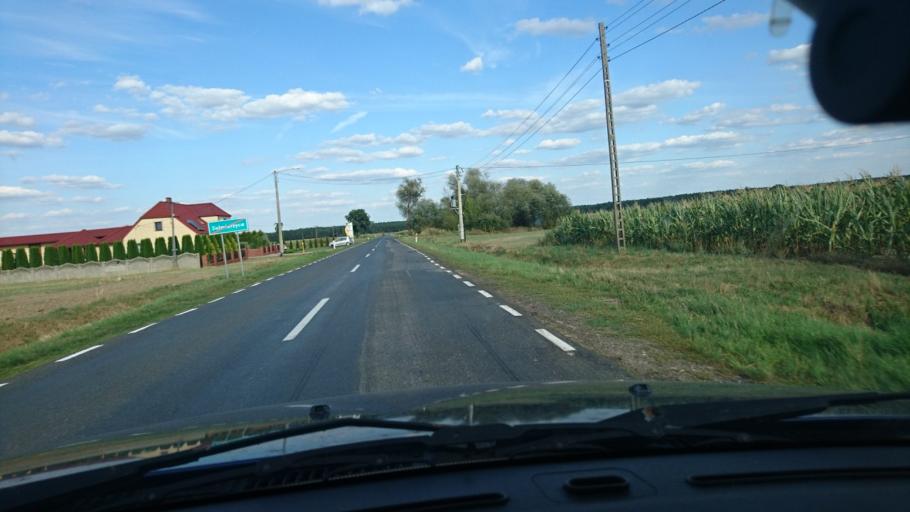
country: PL
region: Greater Poland Voivodeship
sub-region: Powiat krotoszynski
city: Sulmierzyce
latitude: 51.6052
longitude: 17.5539
